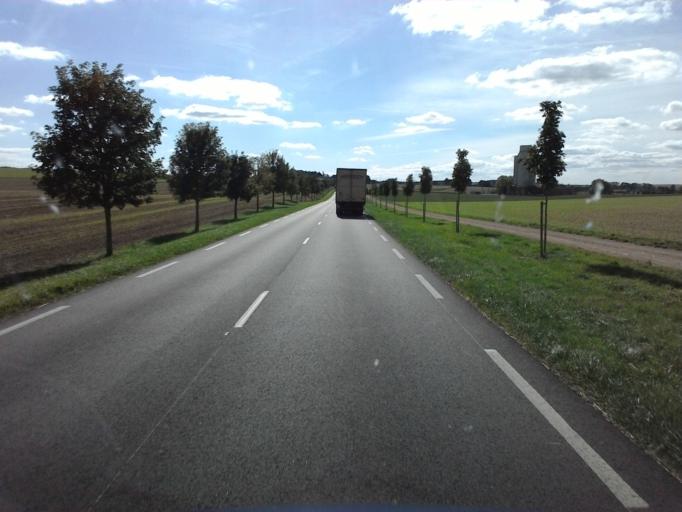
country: FR
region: Bourgogne
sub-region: Departement de la Cote-d'Or
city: Chatillon-sur-Seine
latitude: 47.7375
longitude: 4.4766
